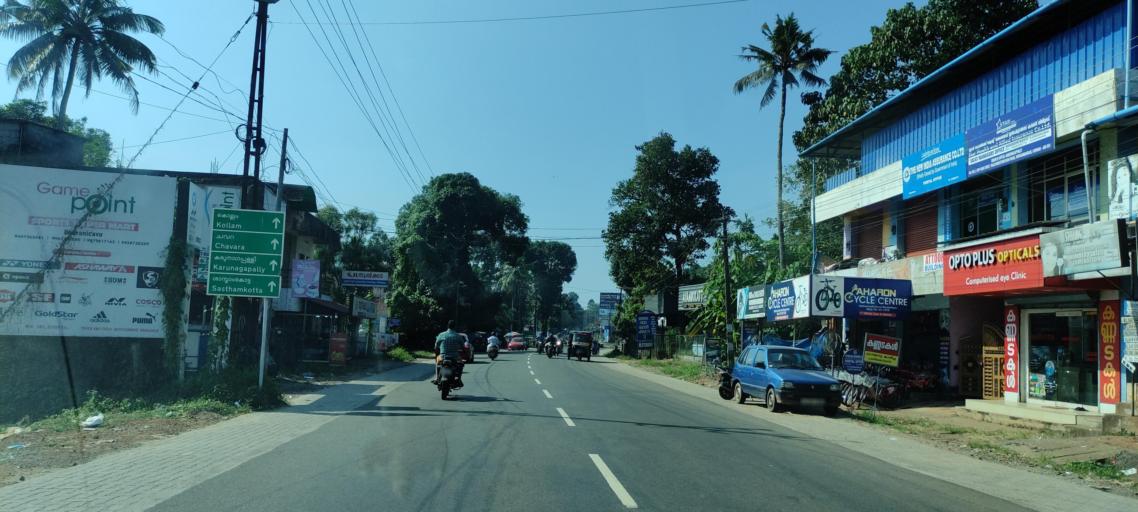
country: IN
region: Kerala
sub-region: Kollam
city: Panmana
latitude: 9.0577
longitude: 76.6375
